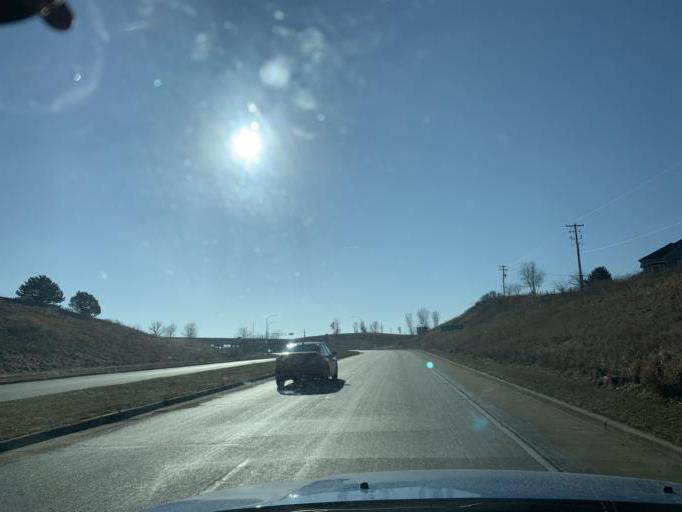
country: US
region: Wisconsin
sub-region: Dane County
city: Verona
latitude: 42.9782
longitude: -89.5140
